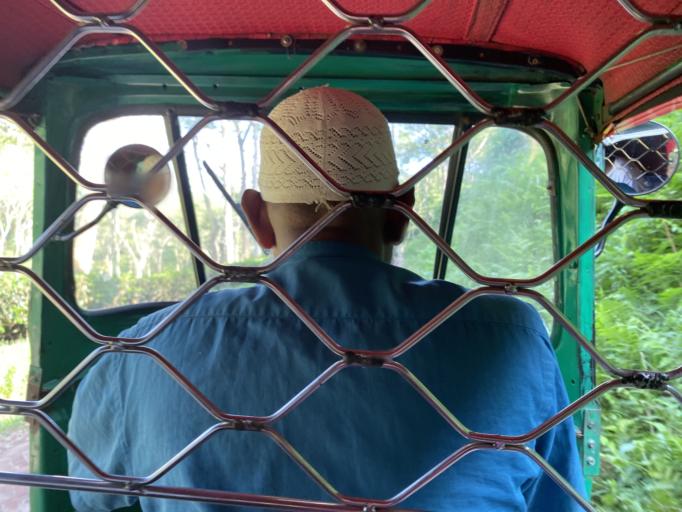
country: IN
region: Tripura
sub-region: Dhalai
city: Kamalpur
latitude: 24.3018
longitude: 91.7936
